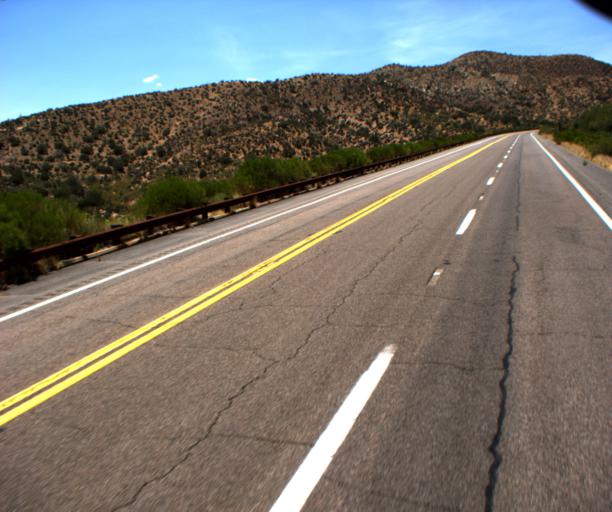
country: US
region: Arizona
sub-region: Gila County
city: Claypool
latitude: 33.5194
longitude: -110.8859
